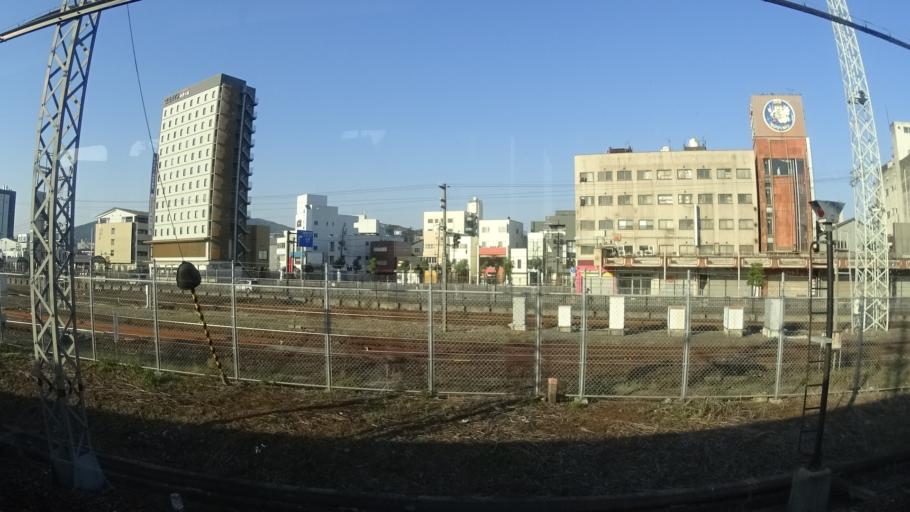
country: JP
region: Mie
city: Ise
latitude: 34.4925
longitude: 136.7086
